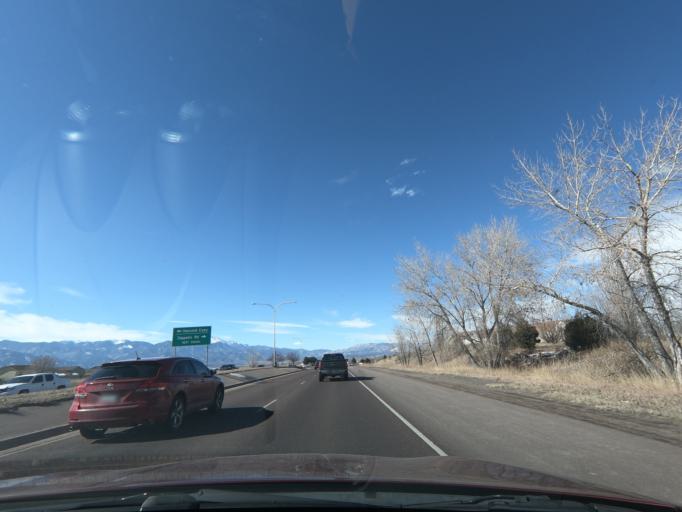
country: US
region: Colorado
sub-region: El Paso County
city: Security-Widefield
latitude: 38.7872
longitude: -104.7260
